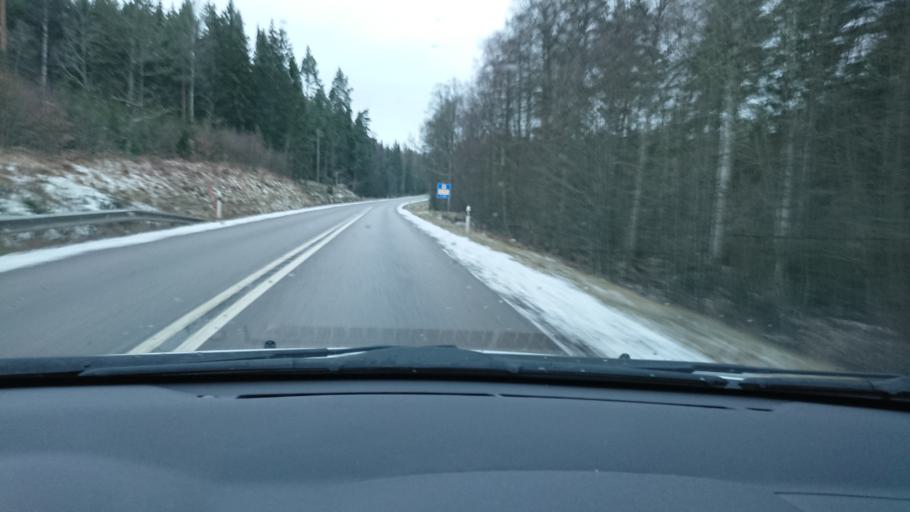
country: SE
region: Kalmar
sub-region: Hultsfreds Kommun
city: Hultsfred
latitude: 57.4928
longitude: 15.8229
